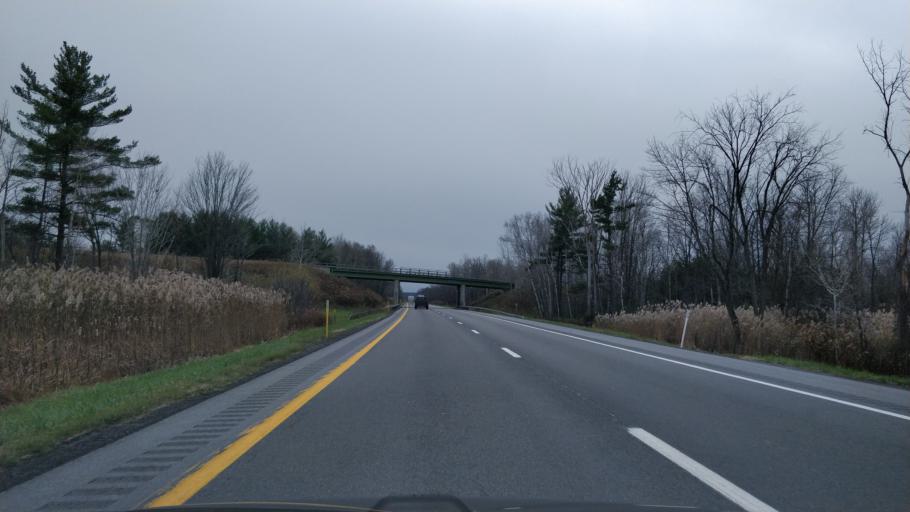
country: US
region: New York
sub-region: Jefferson County
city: Adams
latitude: 43.7949
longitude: -76.0418
